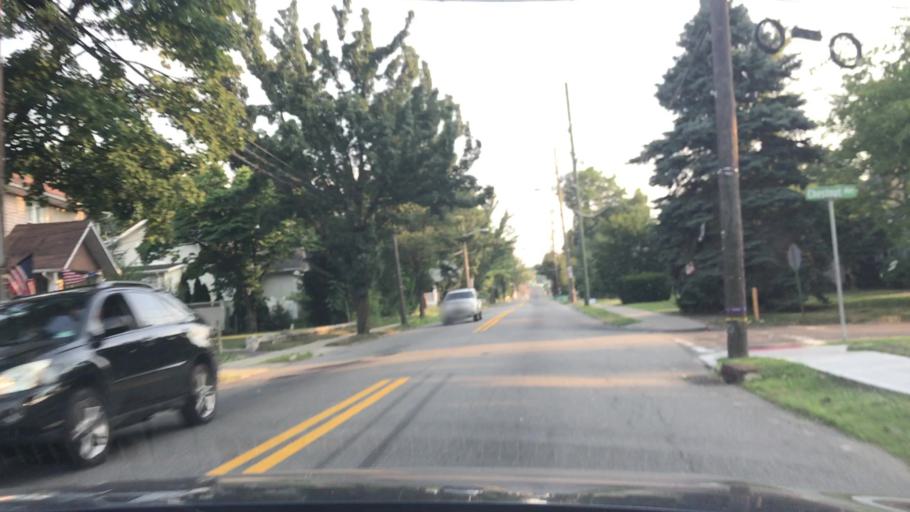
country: US
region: New Jersey
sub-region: Bergen County
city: Emerson
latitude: 40.9794
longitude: -74.0244
